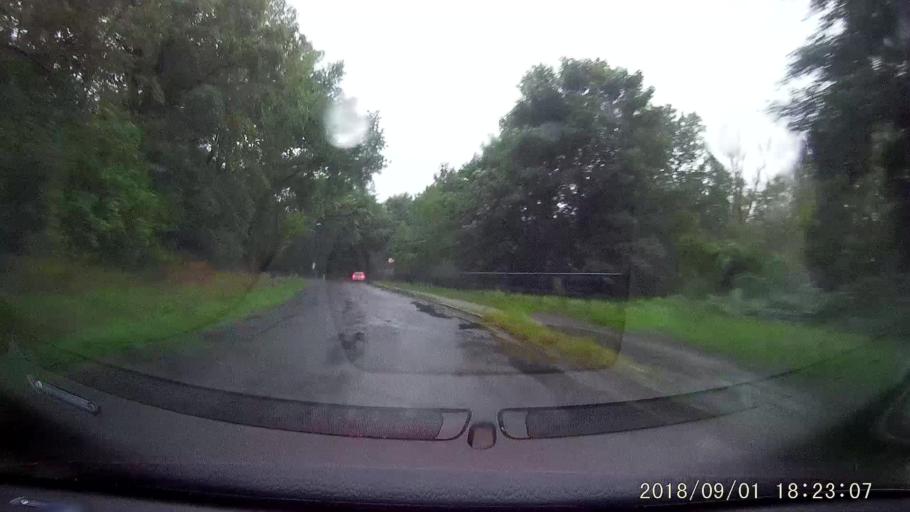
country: PL
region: Lower Silesian Voivodeship
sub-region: Powiat zgorzelecki
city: Piensk
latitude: 51.2459
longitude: 15.0399
